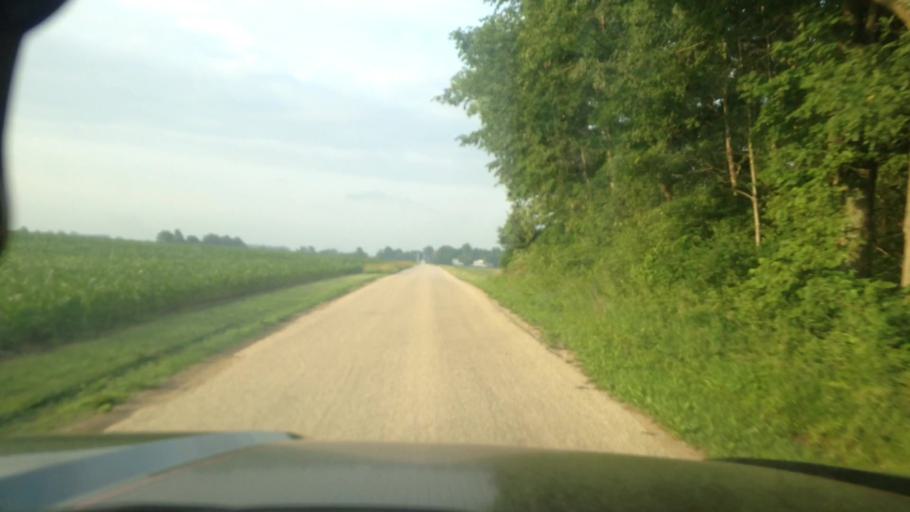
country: US
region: Indiana
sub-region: Randolph County
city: Union City
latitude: 40.2506
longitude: -84.8624
